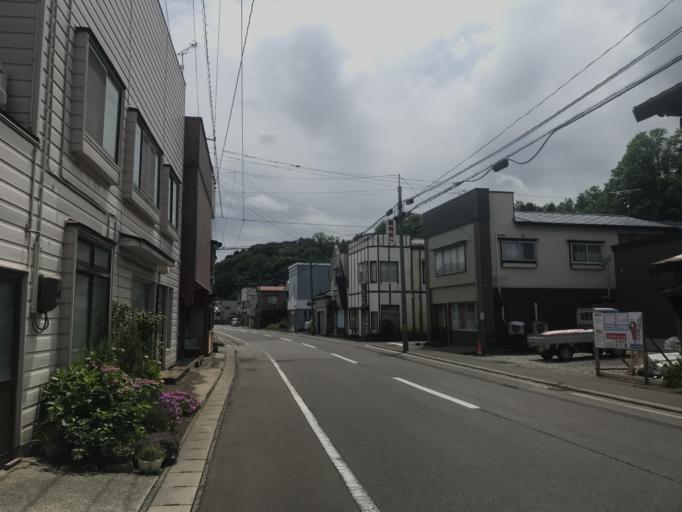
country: JP
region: Aomori
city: Shimokizukuri
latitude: 40.7796
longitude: 140.2075
